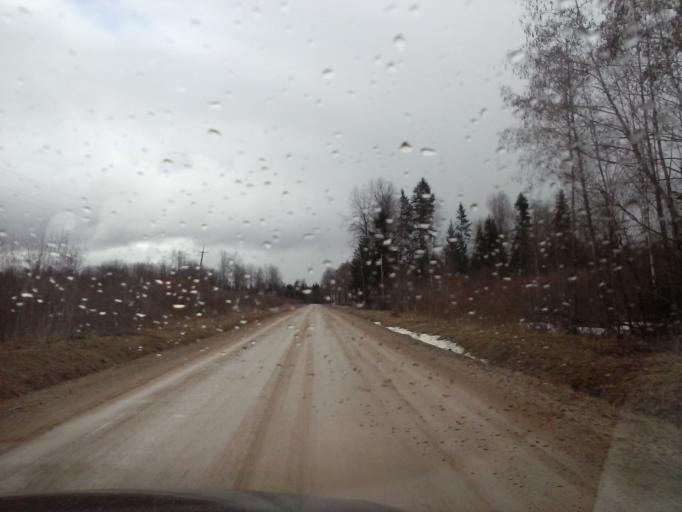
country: EE
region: Jogevamaa
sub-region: Mustvee linn
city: Mustvee
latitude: 59.0948
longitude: 26.9018
